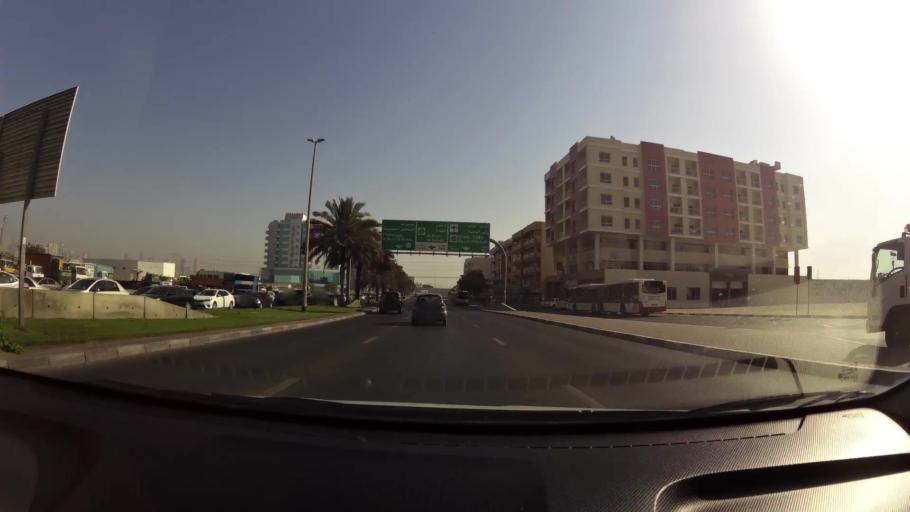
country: AE
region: Ash Shariqah
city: Sharjah
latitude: 25.2940
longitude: 55.3959
